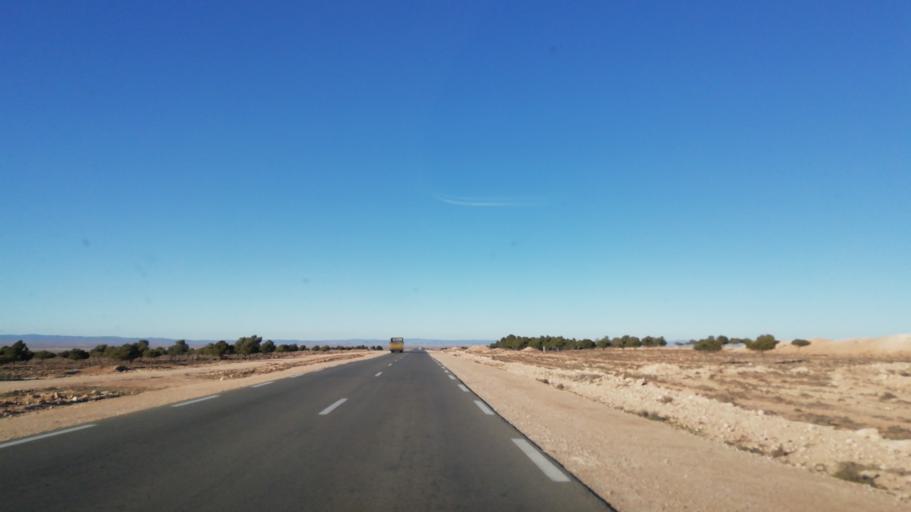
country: DZ
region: Tlemcen
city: Sebdou
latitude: 34.2858
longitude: -1.2596
